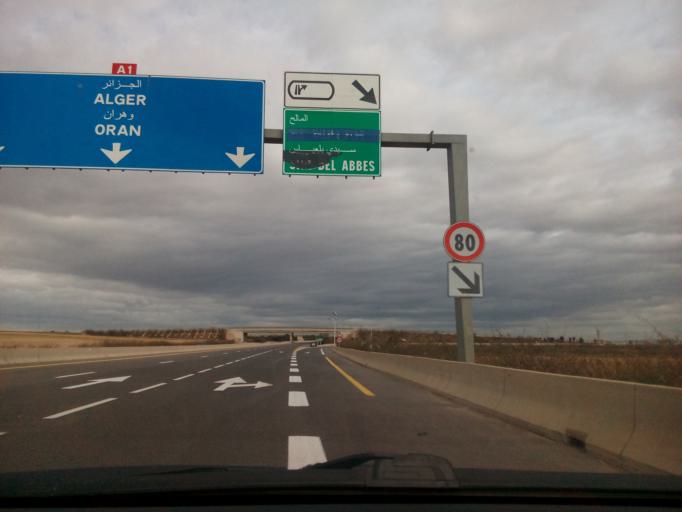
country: DZ
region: Sidi Bel Abbes
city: Sidi Bel Abbes
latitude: 35.2177
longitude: -0.6774
